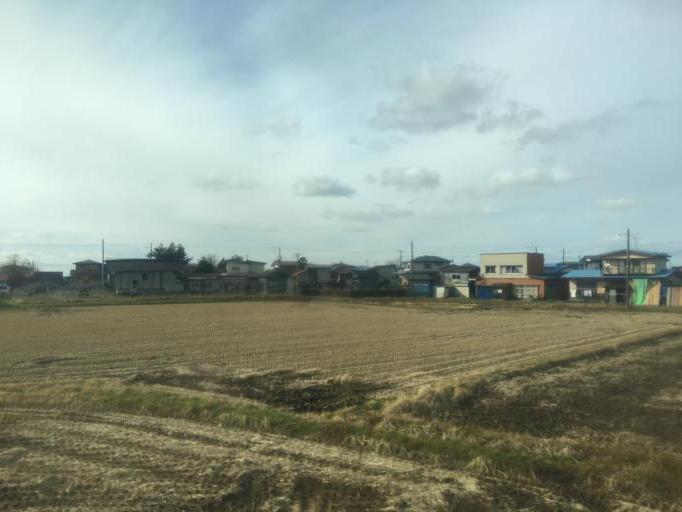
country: JP
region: Akita
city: Tenno
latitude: 39.9575
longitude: 140.0760
